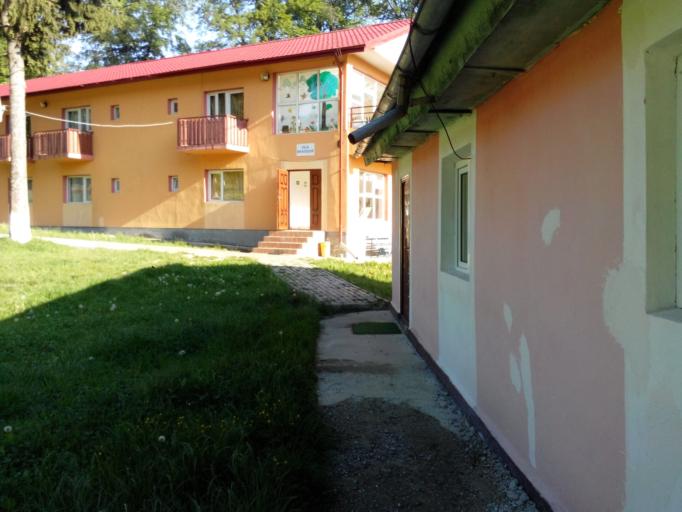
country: RO
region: Iasi
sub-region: Comuna Mogosesti-Siret
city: Muncelu de Sus
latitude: 47.1339
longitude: 26.7472
